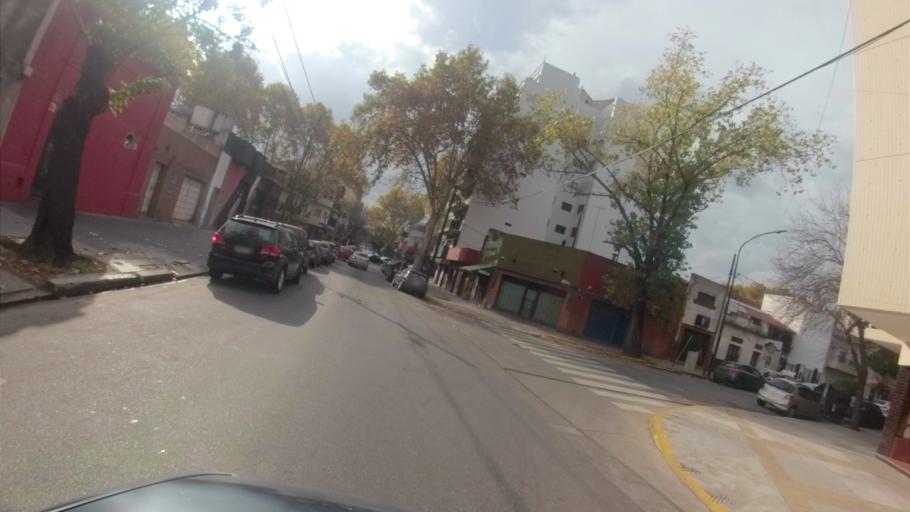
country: AR
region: Buenos Aires F.D.
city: Colegiales
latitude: -34.5806
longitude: -58.4722
